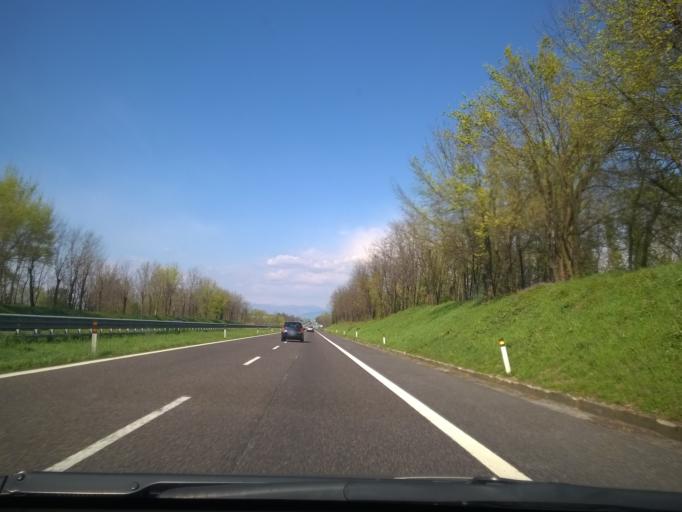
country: IT
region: Lombardy
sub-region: Provincia di Brescia
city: Manerbio
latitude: 45.3510
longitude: 10.1626
